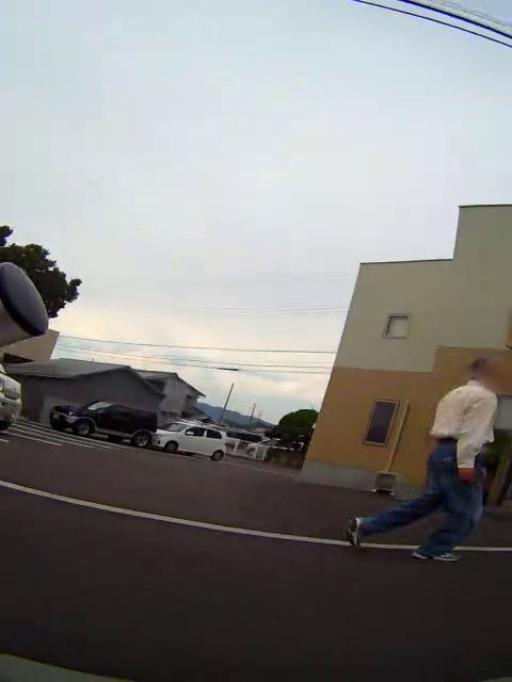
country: JP
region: Hyogo
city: Fukura
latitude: 34.2749
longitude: 134.7635
